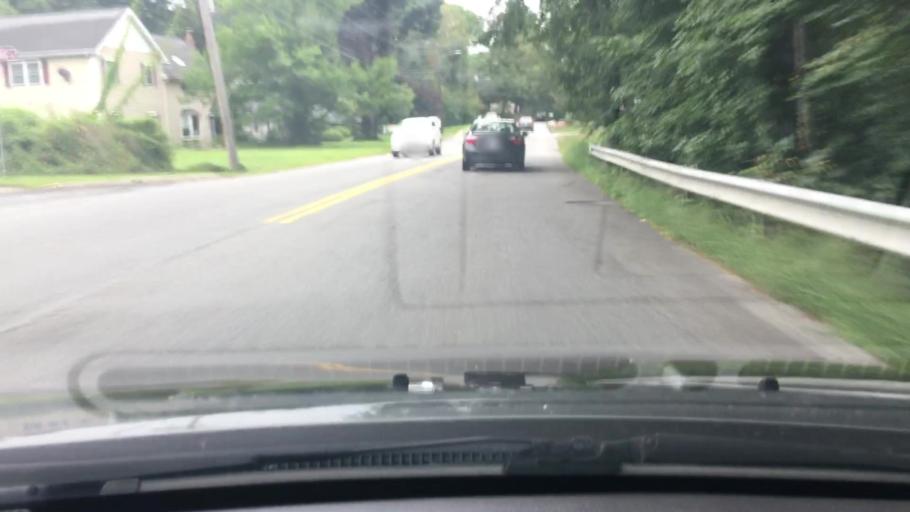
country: US
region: Massachusetts
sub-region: Worcester County
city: Milford
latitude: 42.1595
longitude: -71.5176
